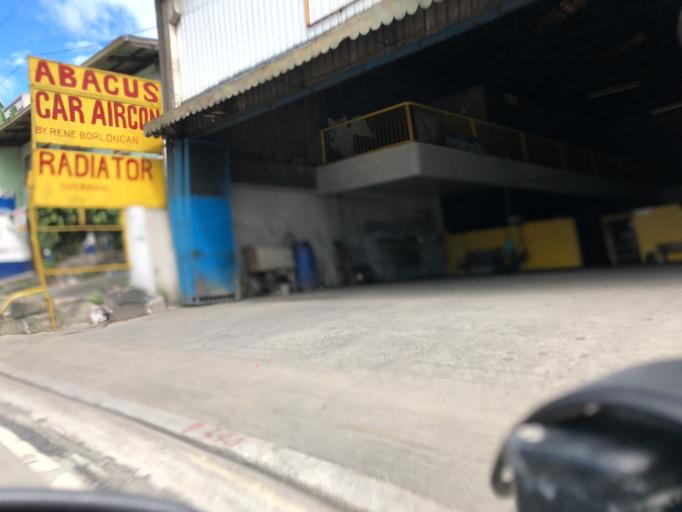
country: PH
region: Calabarzon
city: Bagong Pagasa
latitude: 14.7230
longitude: 121.0612
